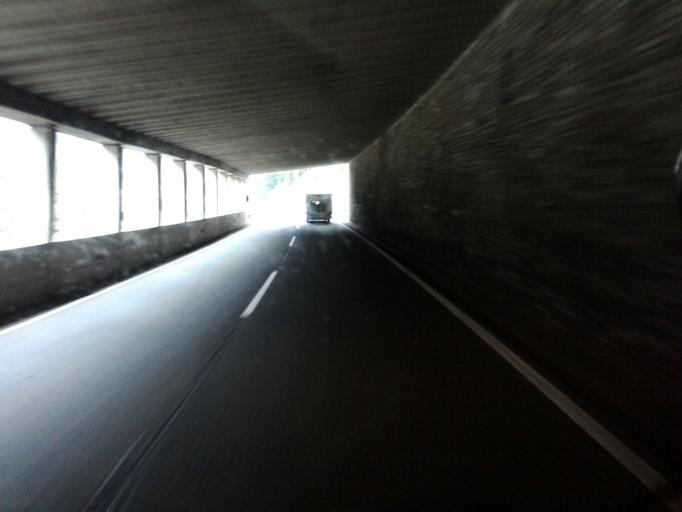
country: AT
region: Tyrol
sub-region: Politischer Bezirk Lienz
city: Matrei in Osttirol
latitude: 47.0338
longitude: 12.5198
